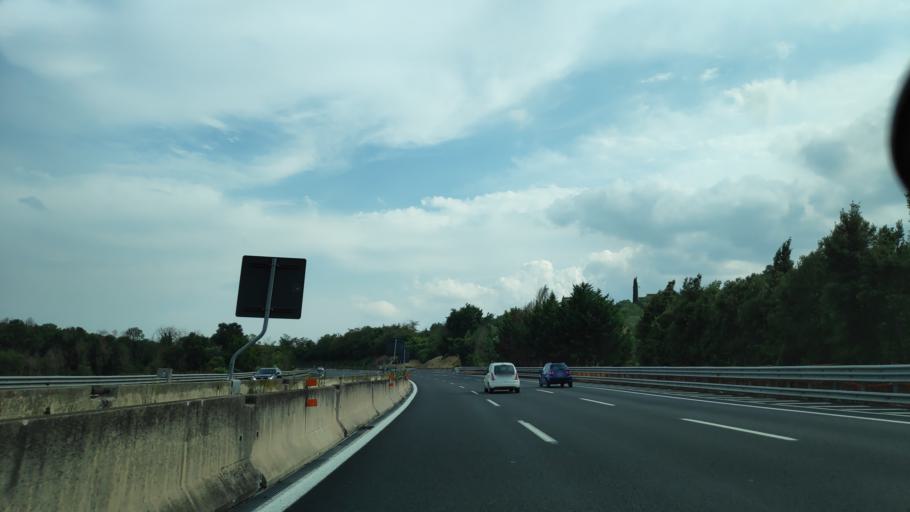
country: IT
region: Latium
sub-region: Citta metropolitana di Roma Capitale
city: Fiano Romano
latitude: 42.1819
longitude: 12.6022
